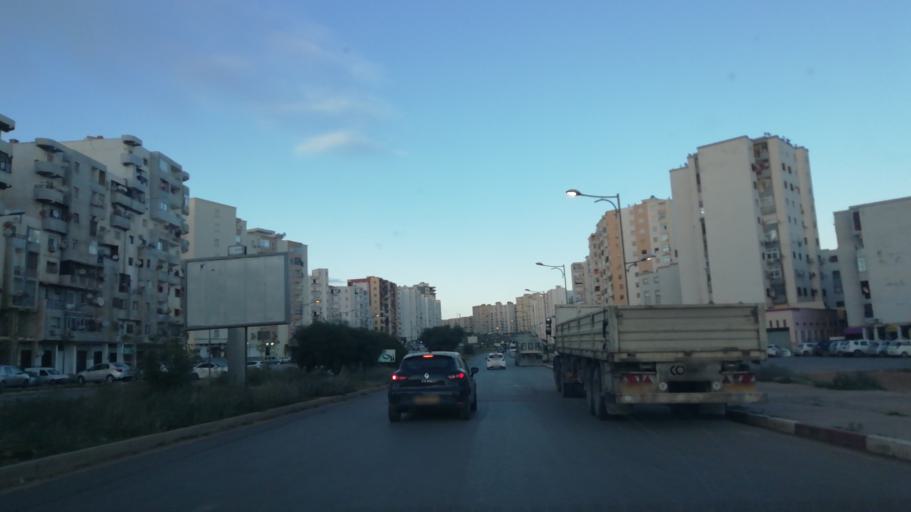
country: DZ
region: Oran
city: Bir el Djir
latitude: 35.6966
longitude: -0.5661
